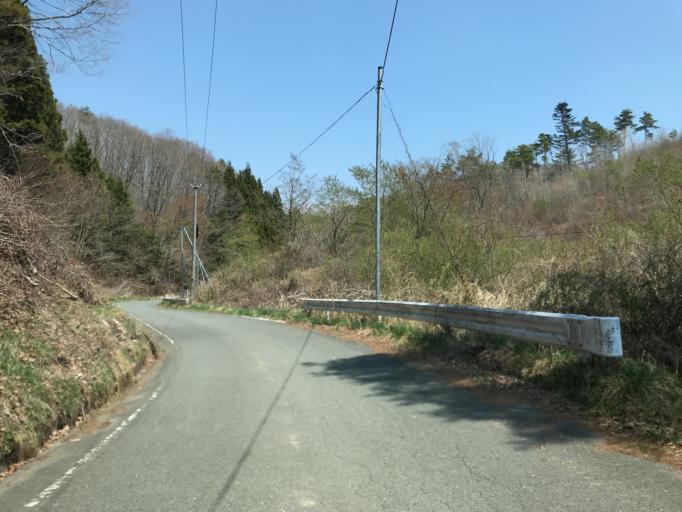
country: JP
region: Fukushima
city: Ishikawa
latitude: 36.9890
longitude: 140.5802
